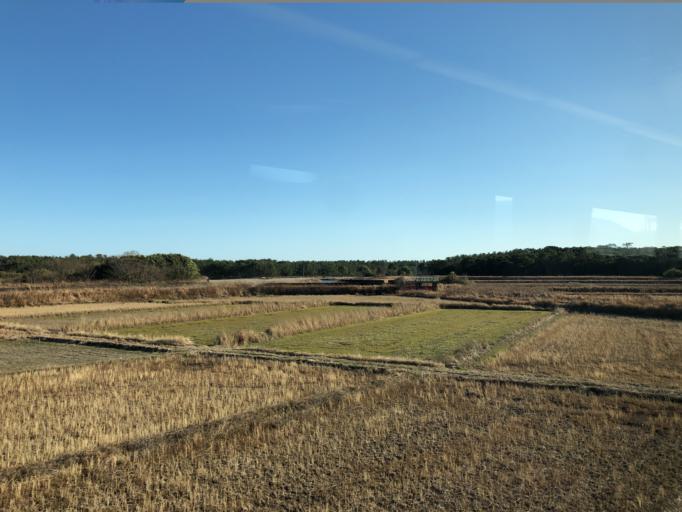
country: JP
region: Kochi
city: Nakamura
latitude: 33.0335
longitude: 133.0185
